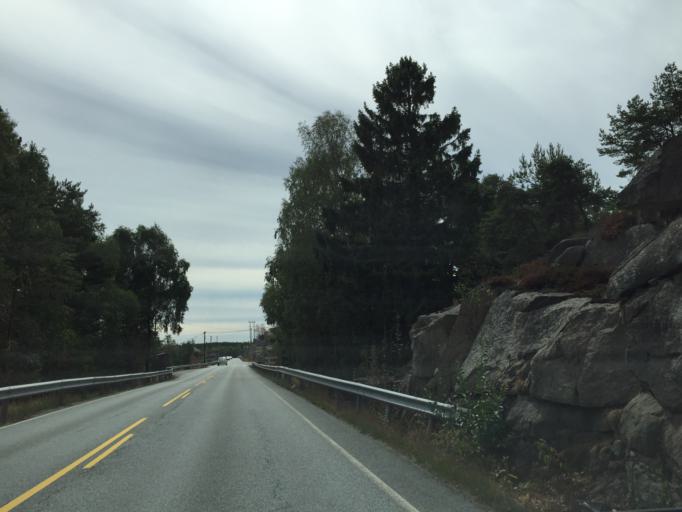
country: NO
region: Ostfold
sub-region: Hvaler
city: Skjaerhalden
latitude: 59.0881
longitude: 10.9261
